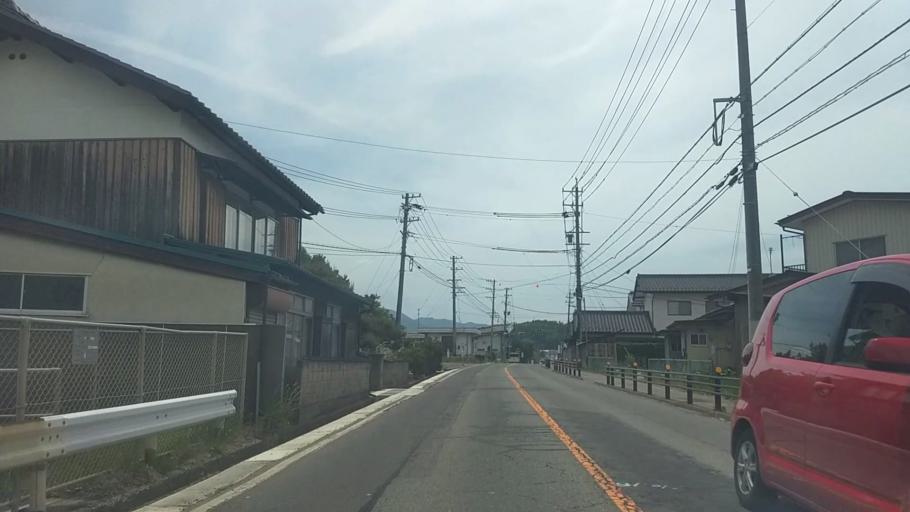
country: JP
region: Nagano
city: Saku
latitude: 36.1857
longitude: 138.4815
